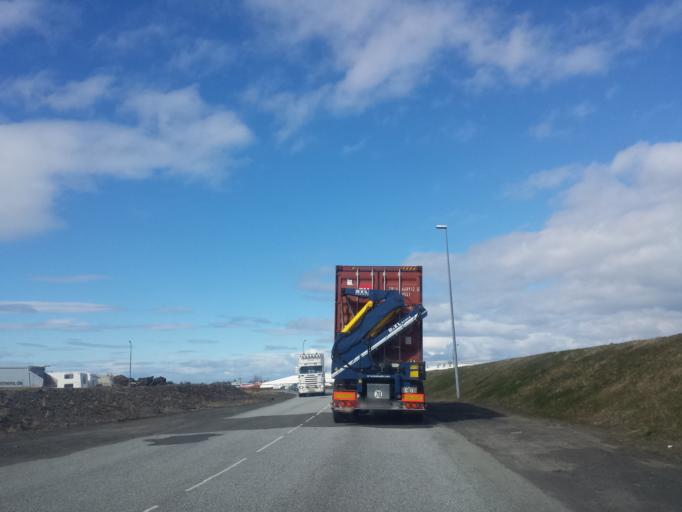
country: IS
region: Capital Region
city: Hafnarfjoerdur
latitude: 64.0765
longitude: -21.9284
